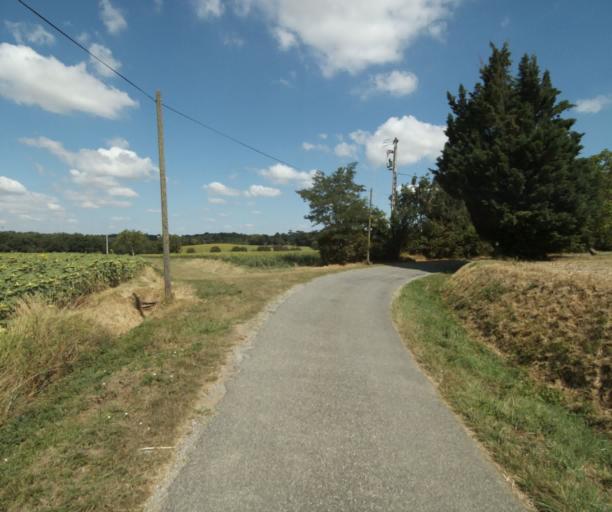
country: FR
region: Midi-Pyrenees
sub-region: Departement de la Haute-Garonne
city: Auriac-sur-Vendinelle
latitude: 43.4546
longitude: 1.8026
